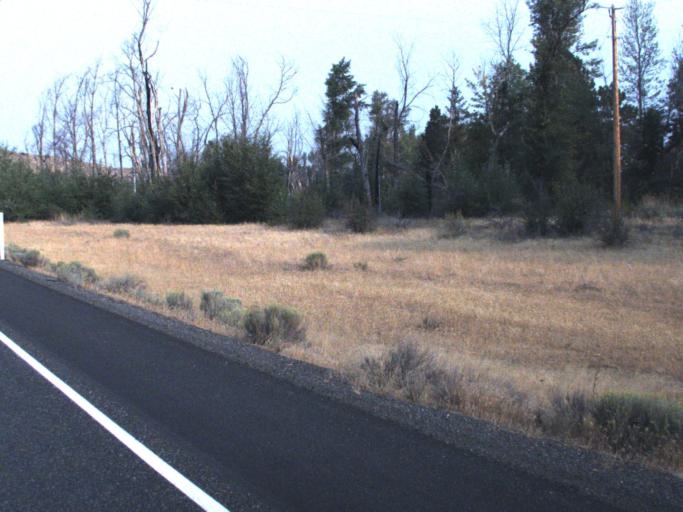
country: US
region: Washington
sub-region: Kittitas County
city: Ellensburg
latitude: 47.0862
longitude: -120.6474
